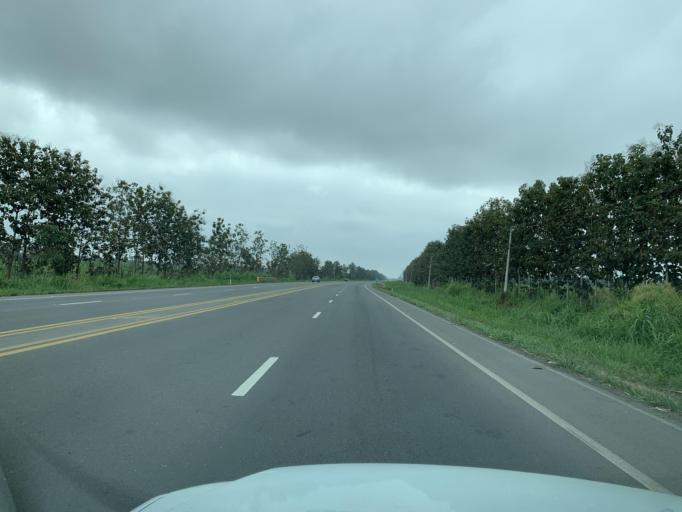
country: EC
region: Guayas
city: Coronel Marcelino Mariduena
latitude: -2.3034
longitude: -79.4862
